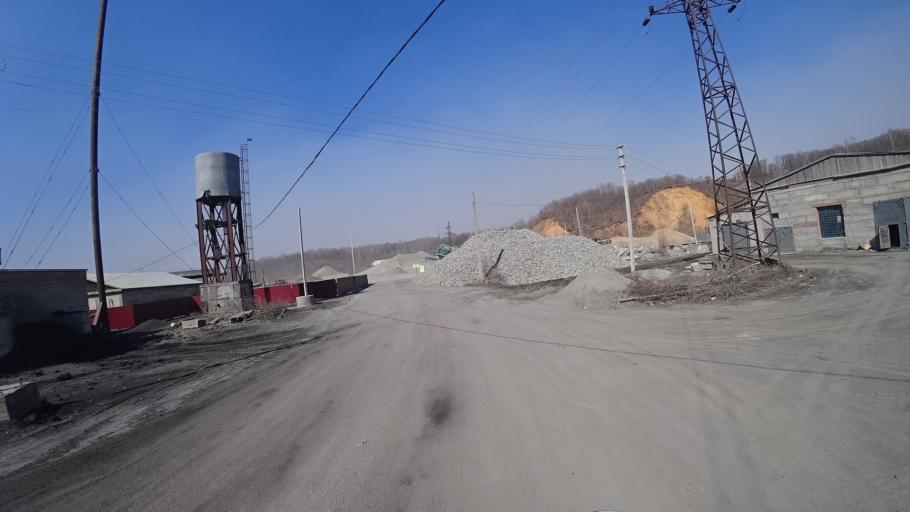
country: RU
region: Amur
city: Novobureyskiy
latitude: 49.7906
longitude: 129.9620
